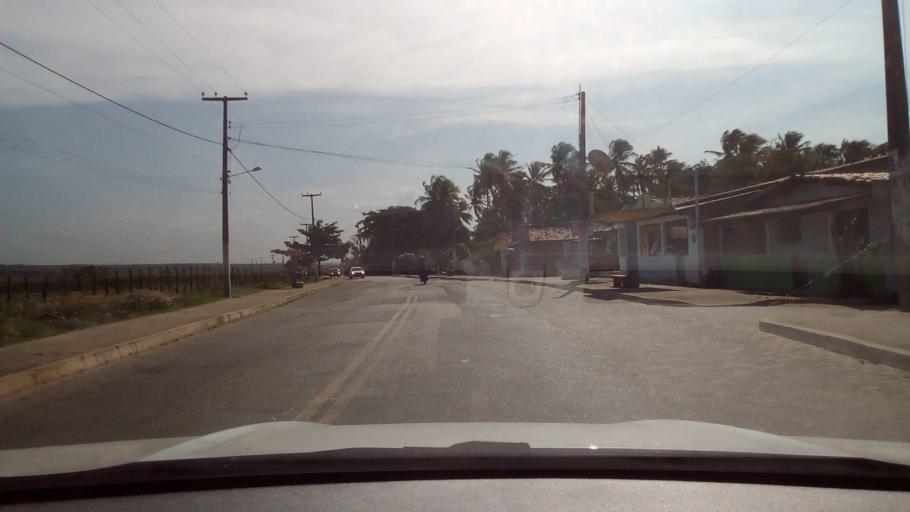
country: BR
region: Rio Grande do Norte
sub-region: Goianinha
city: Goianinha
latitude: -6.2438
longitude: -35.1804
